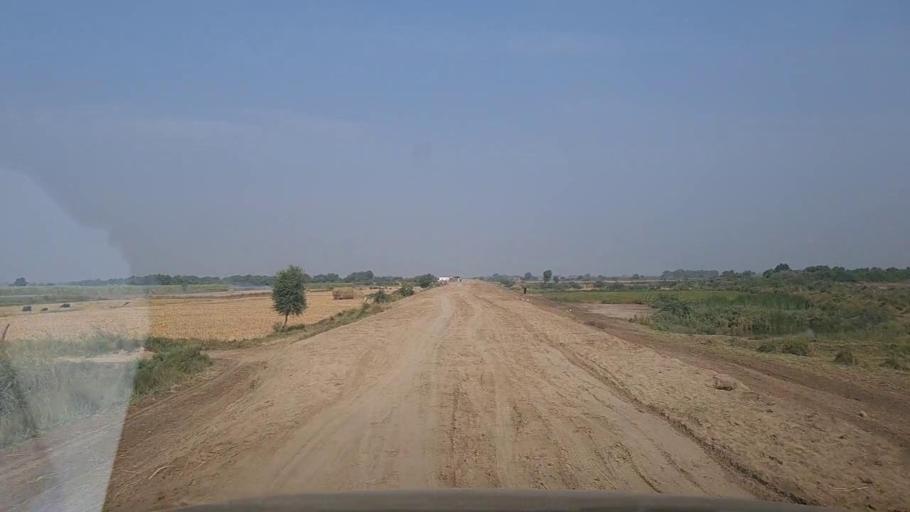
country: PK
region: Sindh
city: Bulri
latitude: 24.9990
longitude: 68.2896
